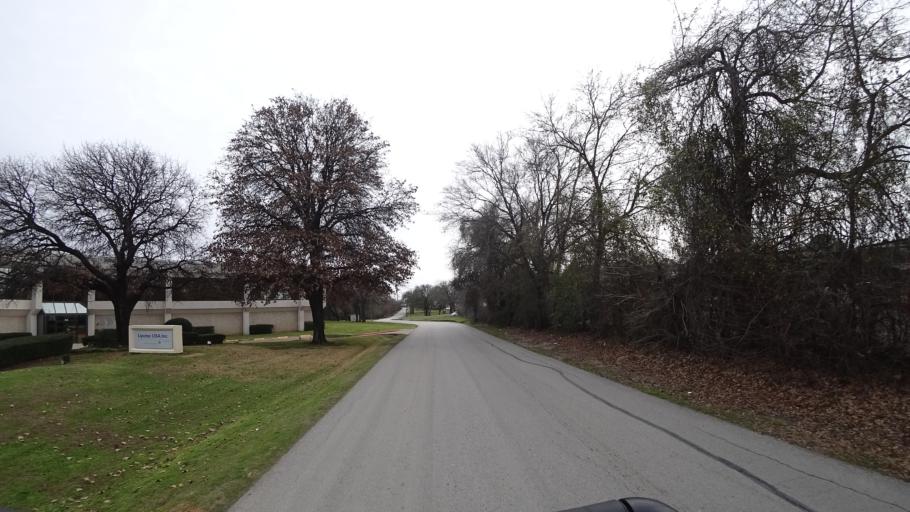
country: US
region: Texas
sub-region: Denton County
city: Lewisville
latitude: 33.0301
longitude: -96.9875
